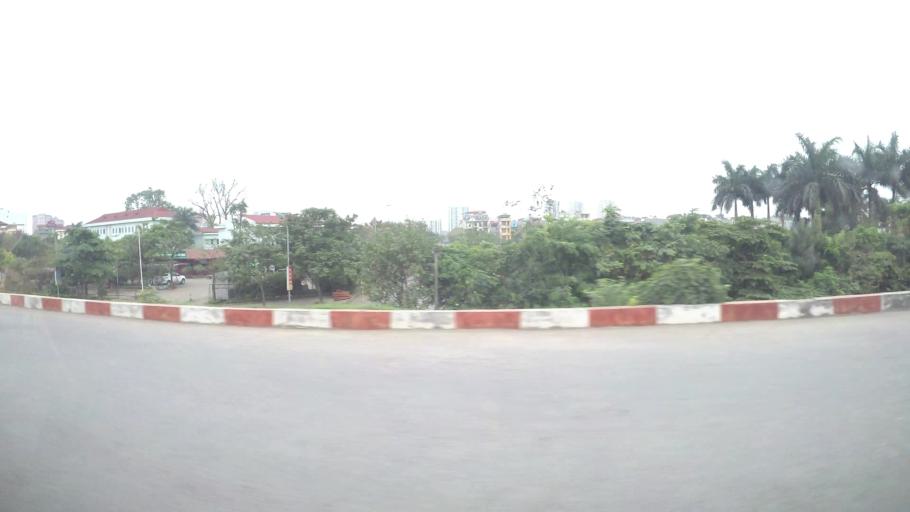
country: VN
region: Ha Noi
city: Trau Quy
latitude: 21.0644
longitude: 105.9191
